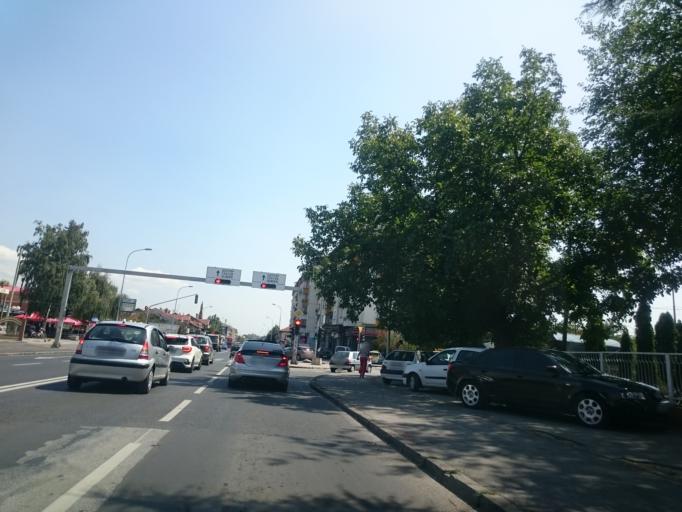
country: MK
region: Saraj
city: Saraj
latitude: 42.0062
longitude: 21.3501
